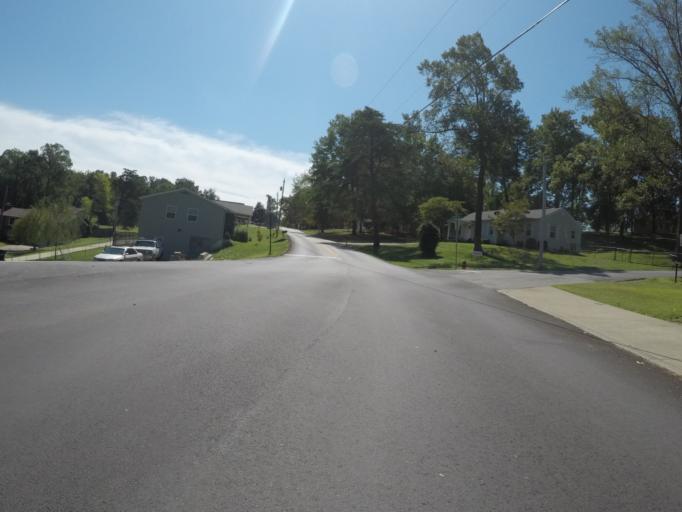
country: US
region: Kentucky
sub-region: Boyd County
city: Ashland
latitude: 38.4481
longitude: -82.6415
